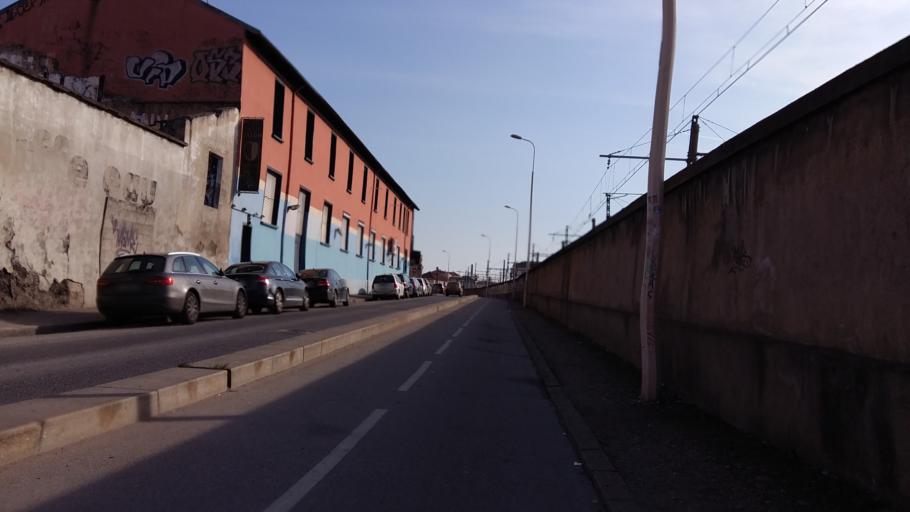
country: FR
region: Rhone-Alpes
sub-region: Departement du Rhone
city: Lyon
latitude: 45.7413
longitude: 4.8483
